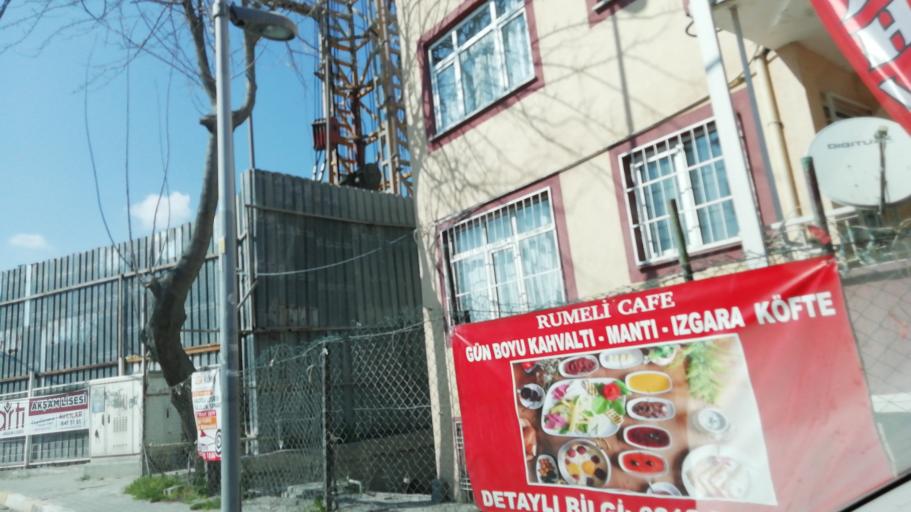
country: TR
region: Istanbul
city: Yakuplu
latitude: 40.9730
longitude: 28.7367
